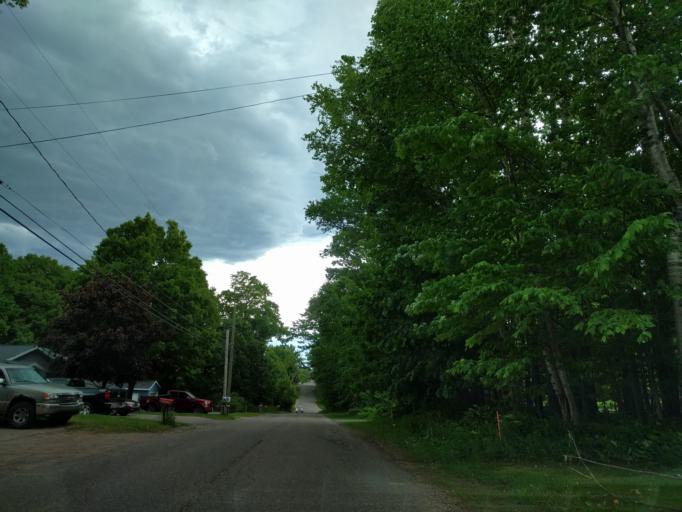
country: US
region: Michigan
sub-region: Marquette County
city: Trowbridge Park
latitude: 46.5570
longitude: -87.4423
